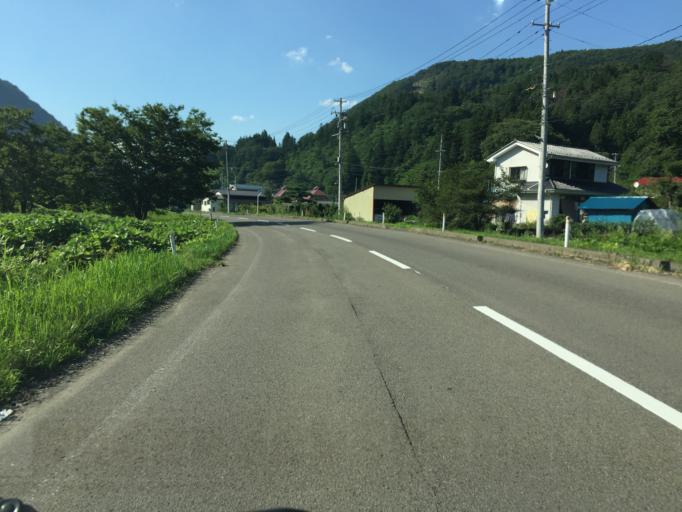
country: JP
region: Fukushima
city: Hobaramachi
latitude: 37.9029
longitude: 140.4318
